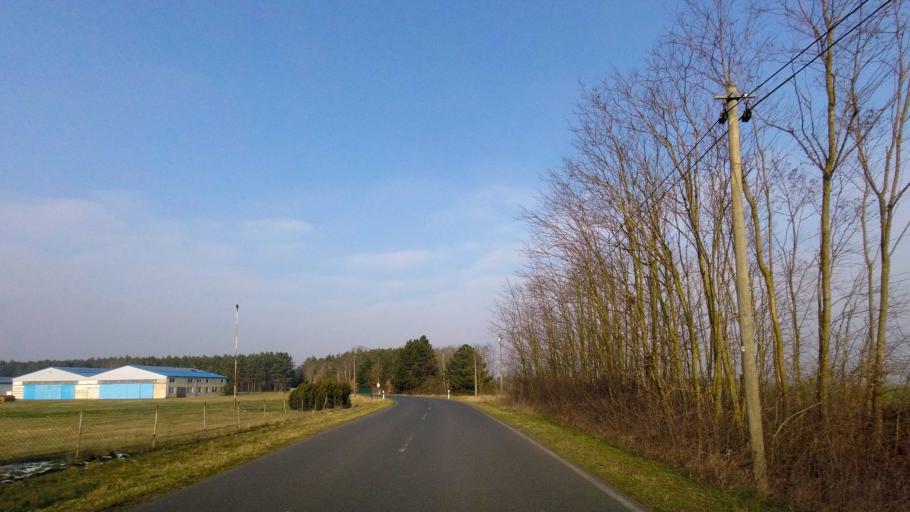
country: DE
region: Brandenburg
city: Juterbog
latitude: 51.9006
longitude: 13.0635
